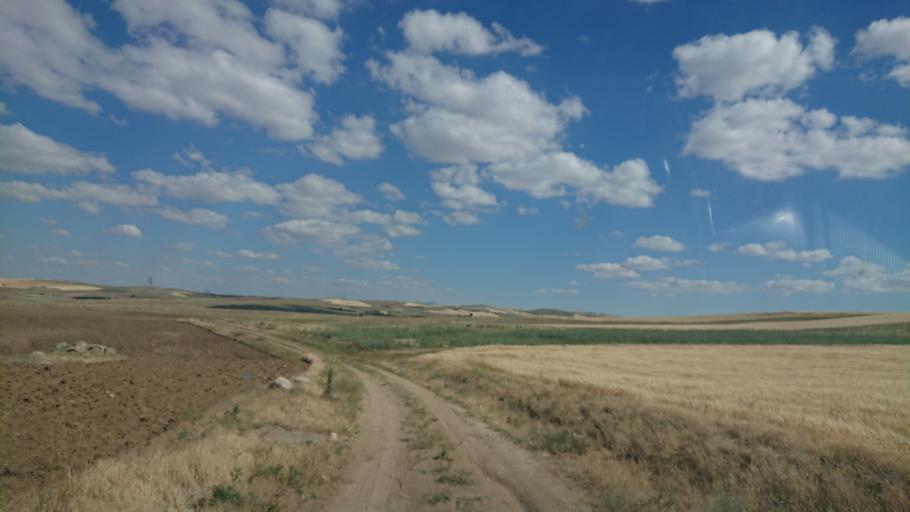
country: TR
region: Aksaray
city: Sariyahsi
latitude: 38.9290
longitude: 33.8494
